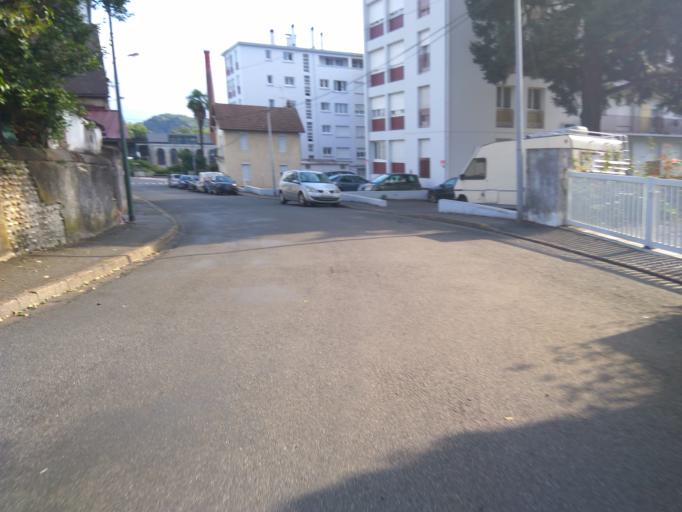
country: FR
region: Aquitaine
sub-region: Departement des Pyrenees-Atlantiques
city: Pau
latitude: 43.2930
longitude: -0.3649
